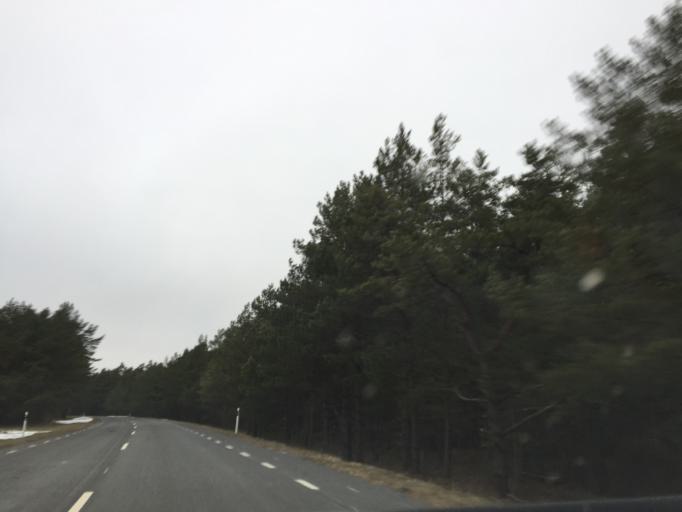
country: EE
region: Saare
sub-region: Kuressaare linn
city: Kuressaare
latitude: 58.5466
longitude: 22.3359
